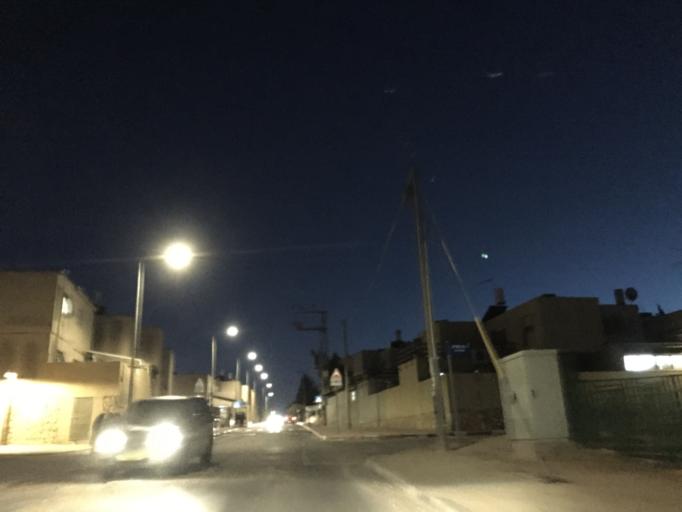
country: IL
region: Southern District
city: Mitzpe Ramon
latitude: 30.6133
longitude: 34.8007
